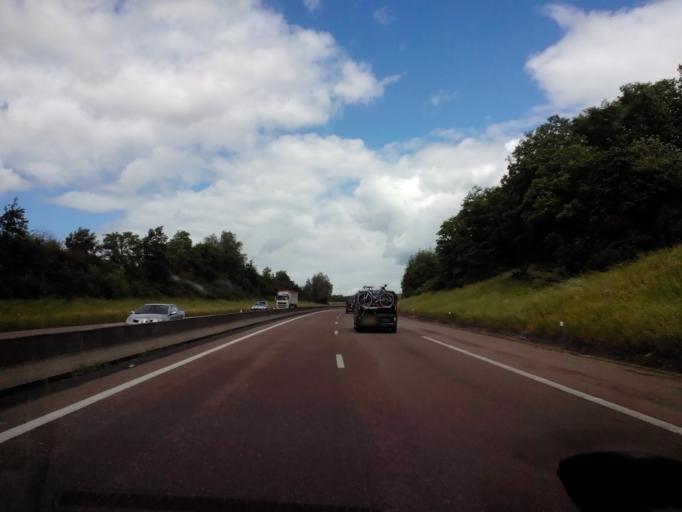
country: FR
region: Lorraine
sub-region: Departement des Vosges
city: Chatenois
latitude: 48.3672
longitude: 5.8697
